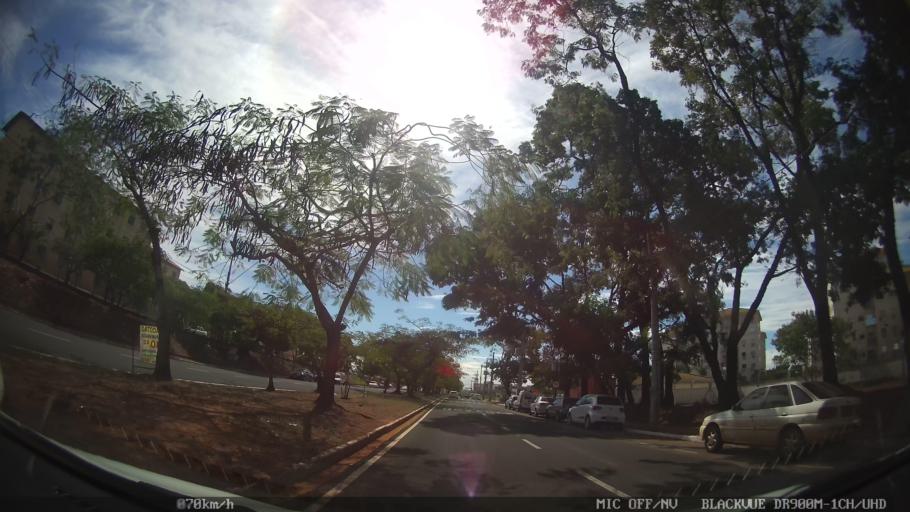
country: BR
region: Sao Paulo
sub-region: Sao Jose Do Rio Preto
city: Sao Jose do Rio Preto
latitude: -20.8271
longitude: -49.3514
